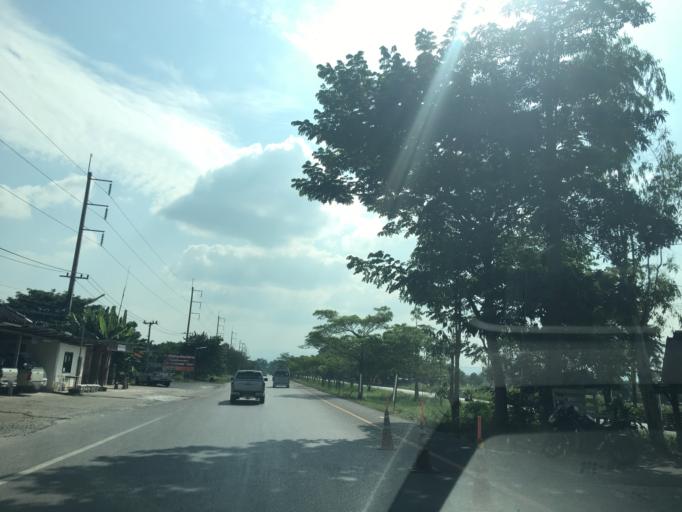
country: TH
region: Chiang Rai
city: Mae Lao
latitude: 19.7319
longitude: 99.7190
